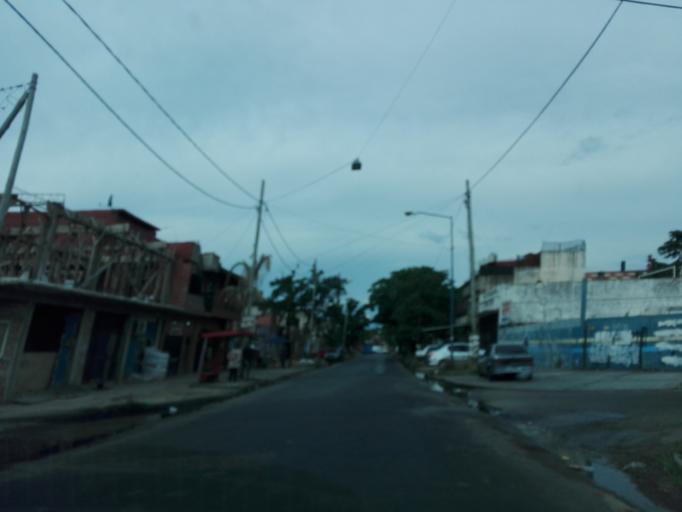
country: AR
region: Buenos Aires
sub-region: Partido de Lanus
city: Lanus
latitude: -34.7061
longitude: -58.3704
